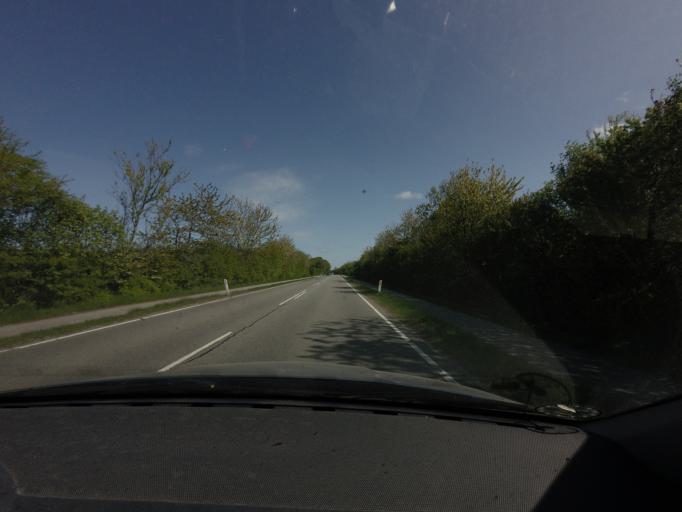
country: DK
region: North Denmark
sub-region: Jammerbugt Kommune
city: Pandrup
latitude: 57.3120
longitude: 9.7055
